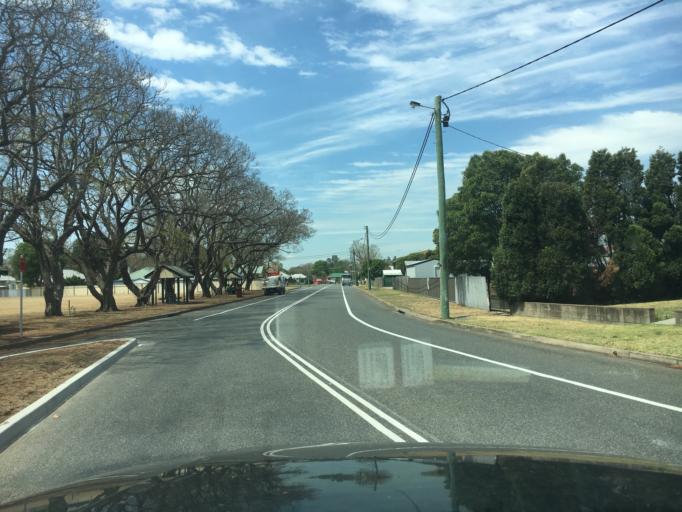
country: AU
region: New South Wales
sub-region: Singleton
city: Singleton
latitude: -32.5722
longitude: 151.1682
